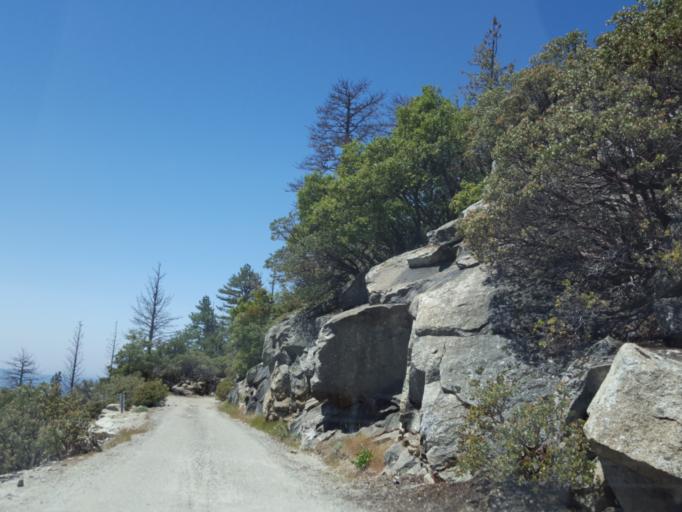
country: US
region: California
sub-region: Madera County
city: Oakhurst
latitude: 37.3175
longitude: -119.4940
